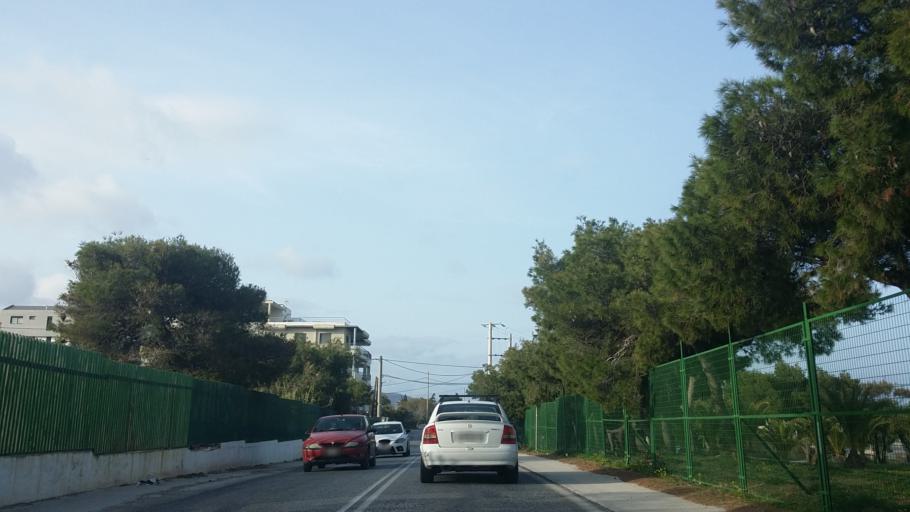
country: GR
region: Attica
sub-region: Nomarchia Anatolikis Attikis
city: Lavrio
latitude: 37.7039
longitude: 24.0543
